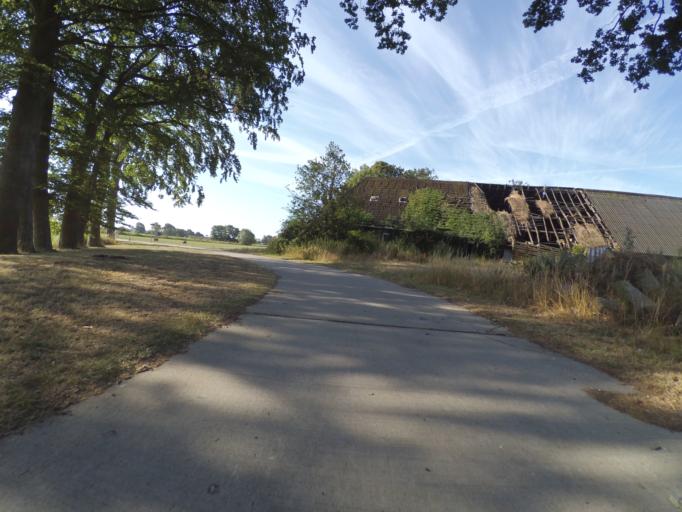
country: NL
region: Gelderland
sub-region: Gemeente Nunspeet
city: Nunspeet
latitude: 52.4045
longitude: 5.7690
